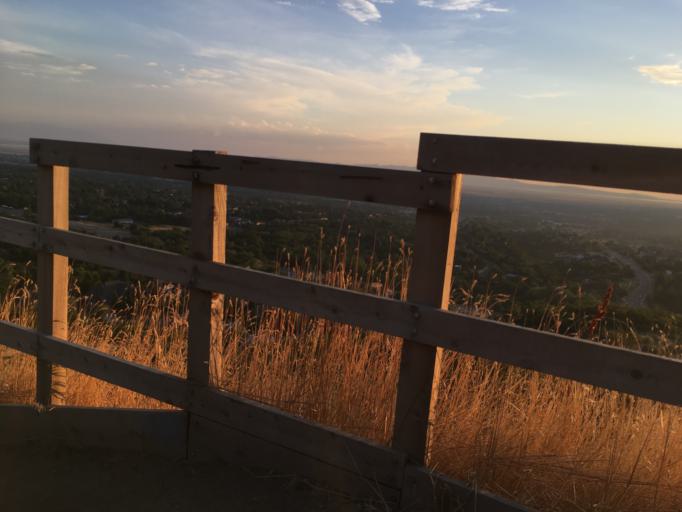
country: US
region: Utah
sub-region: Davis County
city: Fruit Heights
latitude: 41.0665
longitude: -111.9058
